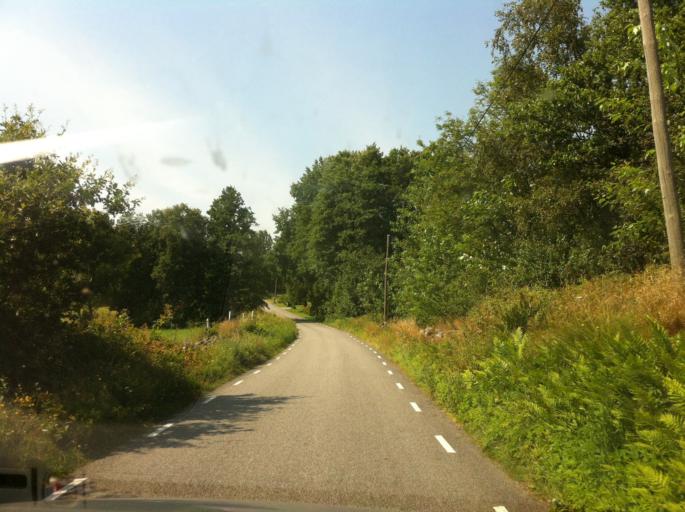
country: SE
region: Skane
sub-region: Hoors Kommun
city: Hoeoer
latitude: 56.0098
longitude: 13.5342
